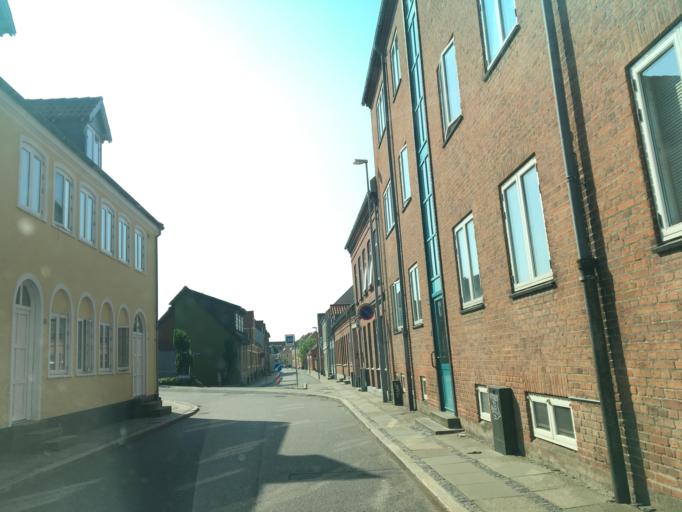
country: DK
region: North Denmark
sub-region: Thisted Kommune
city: Thisted
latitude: 56.9587
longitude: 8.6906
